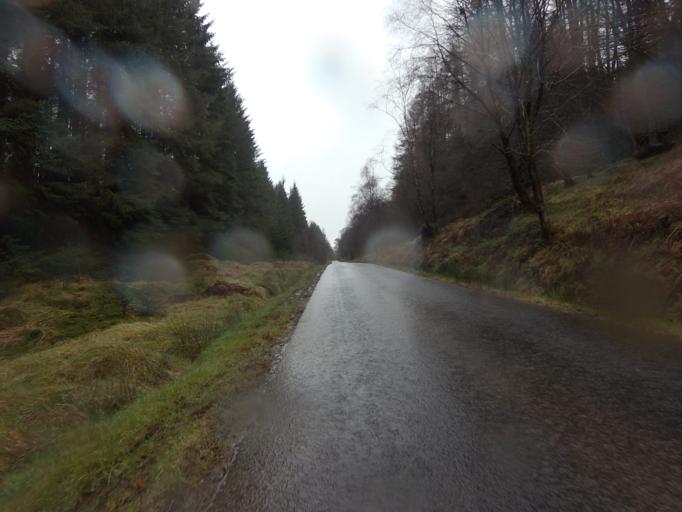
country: GB
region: Scotland
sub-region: West Dunbartonshire
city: Balloch
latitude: 56.2299
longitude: -4.5568
